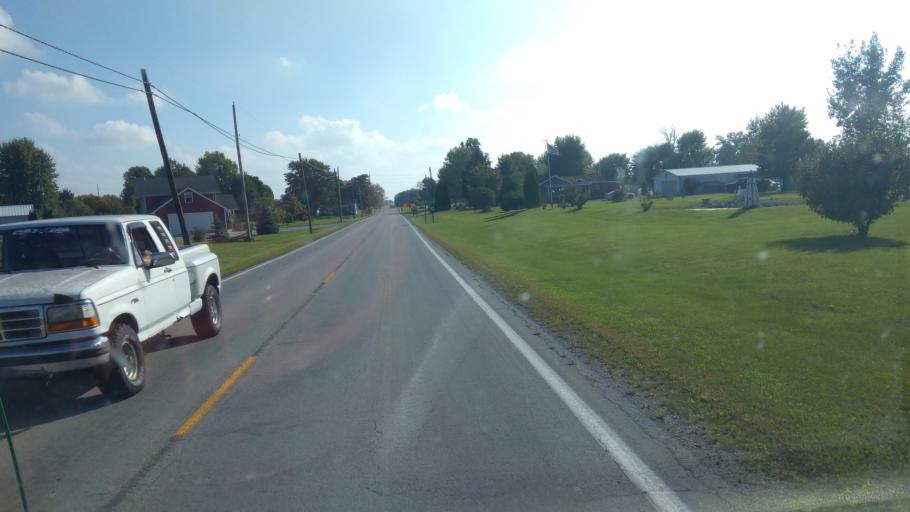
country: US
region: Ohio
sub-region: Hardin County
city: Forest
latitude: 40.7837
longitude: -83.5238
